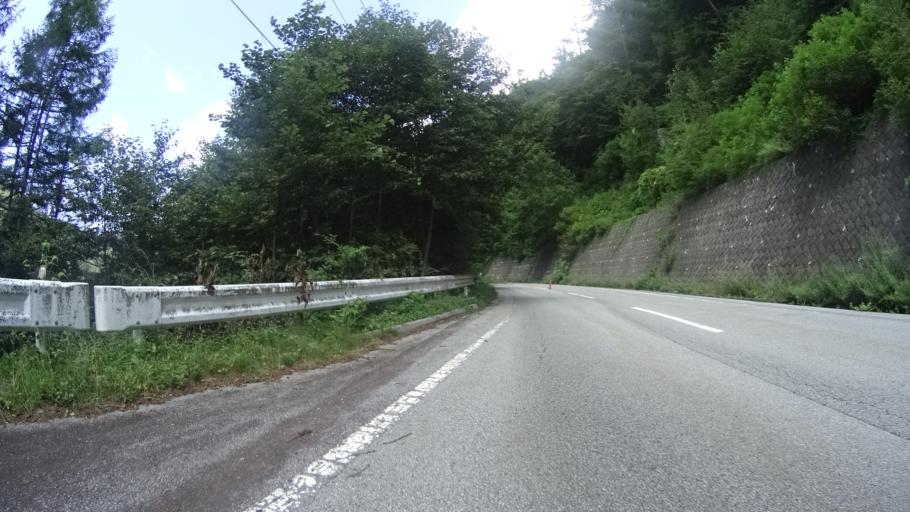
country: JP
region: Yamanashi
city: Enzan
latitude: 35.8038
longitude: 138.6666
